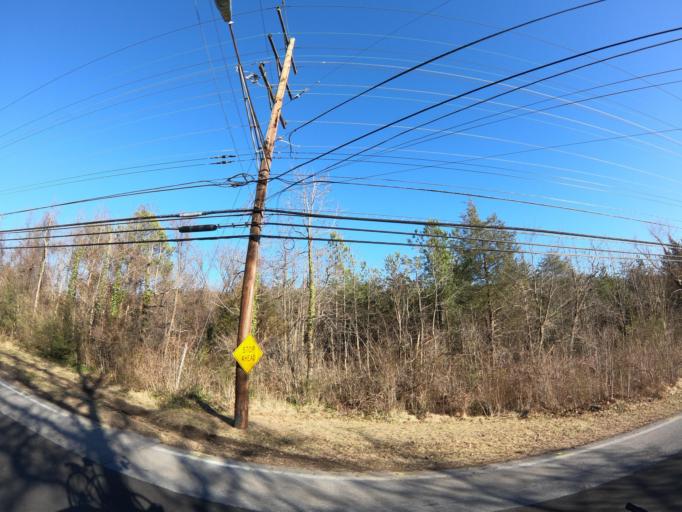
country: US
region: Maryland
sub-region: Prince George's County
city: Berwyn Heights
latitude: 38.9871
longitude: -76.9091
